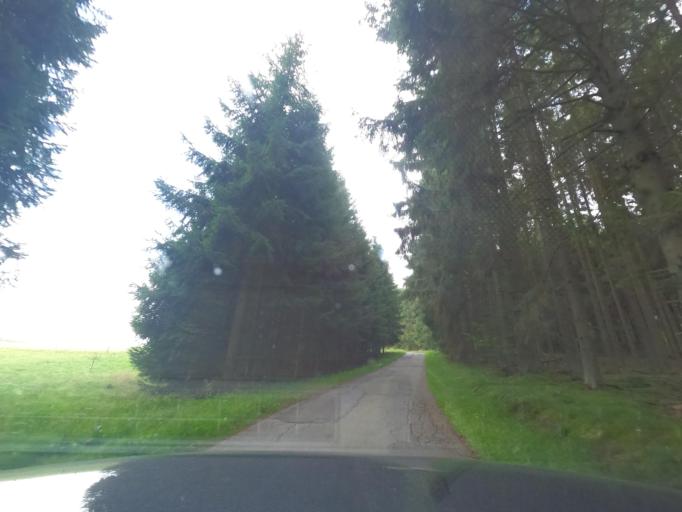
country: DE
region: North Rhine-Westphalia
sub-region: Regierungsbezirk Arnsberg
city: Herscheid
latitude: 51.2044
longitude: 7.7392
